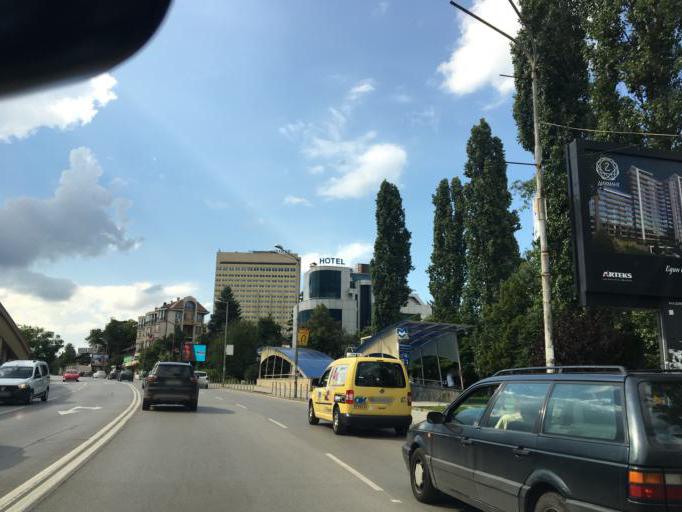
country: BG
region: Sofia-Capital
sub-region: Stolichna Obshtina
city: Sofia
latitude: 42.6714
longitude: 23.3511
